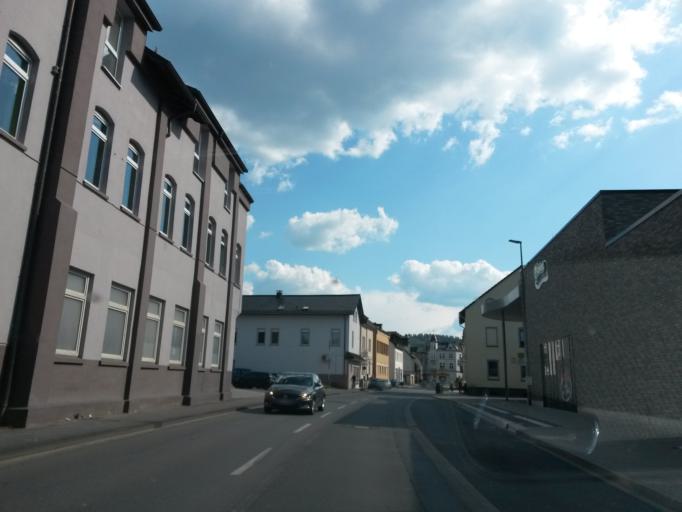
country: DE
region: North Rhine-Westphalia
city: Plettenberg
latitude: 51.2172
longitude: 7.8732
